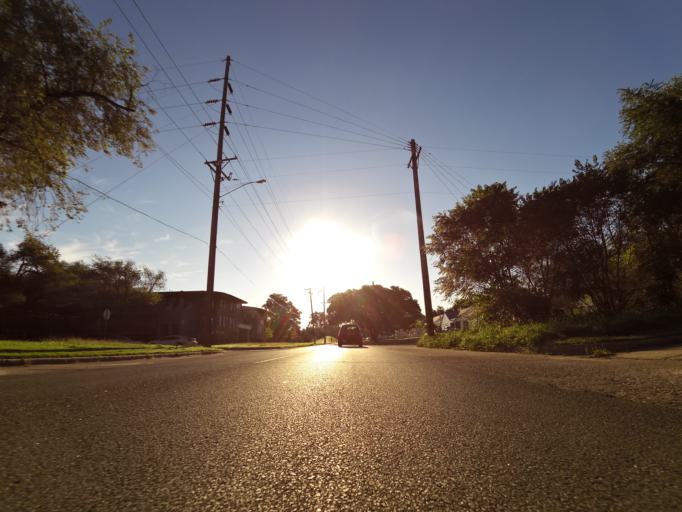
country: US
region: Kansas
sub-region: Sedgwick County
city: Wichita
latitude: 37.7009
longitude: -97.3040
